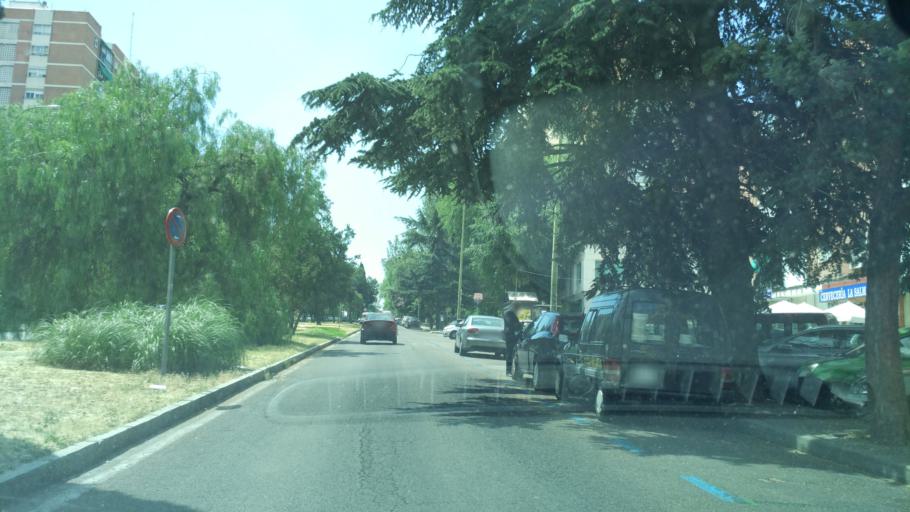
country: ES
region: Madrid
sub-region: Provincia de Madrid
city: Tetuan de las Victorias
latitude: 40.4784
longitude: -3.7040
